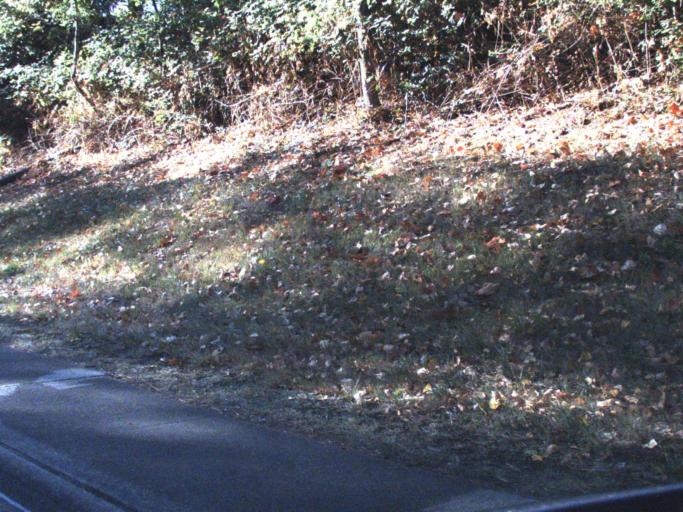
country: US
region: Washington
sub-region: King County
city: Renton
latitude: 47.4543
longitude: -122.2047
